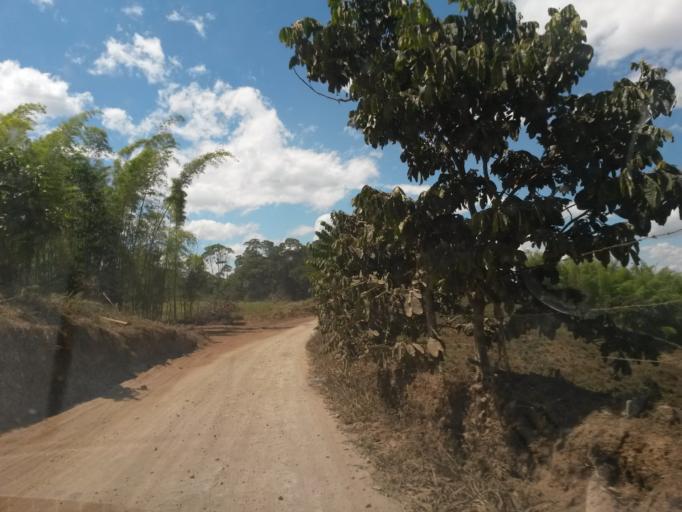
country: CO
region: Cauca
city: Morales
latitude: 2.7411
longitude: -76.6215
